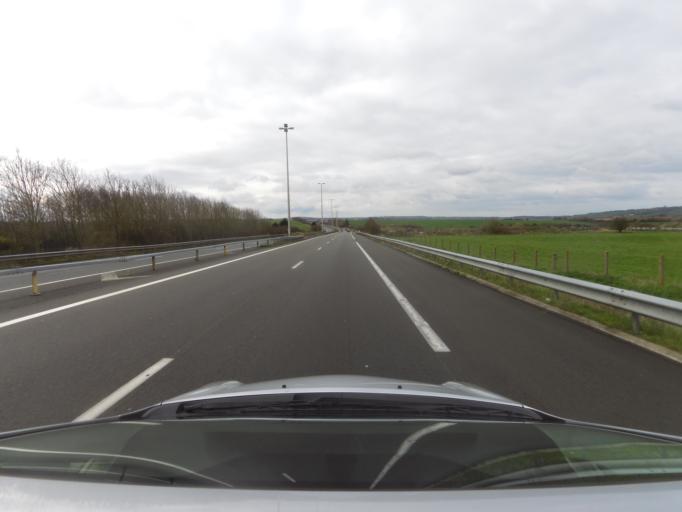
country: FR
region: Nord-Pas-de-Calais
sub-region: Departement du Pas-de-Calais
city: Marquise
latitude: 50.8351
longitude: 1.7050
